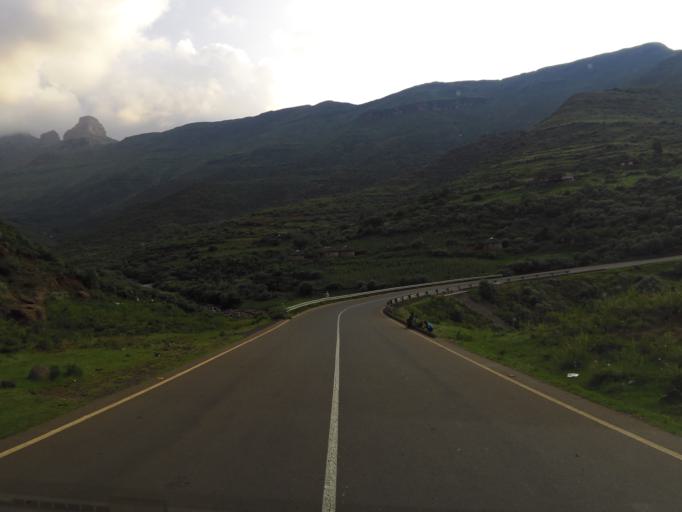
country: LS
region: Butha-Buthe
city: Butha-Buthe
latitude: -29.0472
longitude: 28.3130
